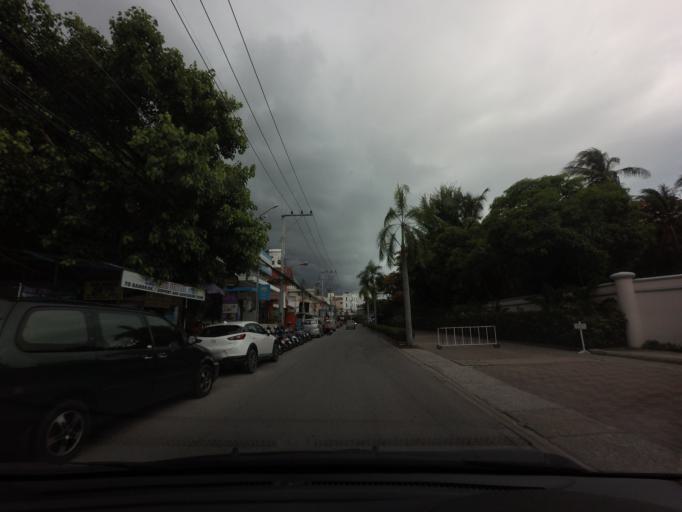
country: TH
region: Prachuap Khiri Khan
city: Hua Hin
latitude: 12.5678
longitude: 99.9600
